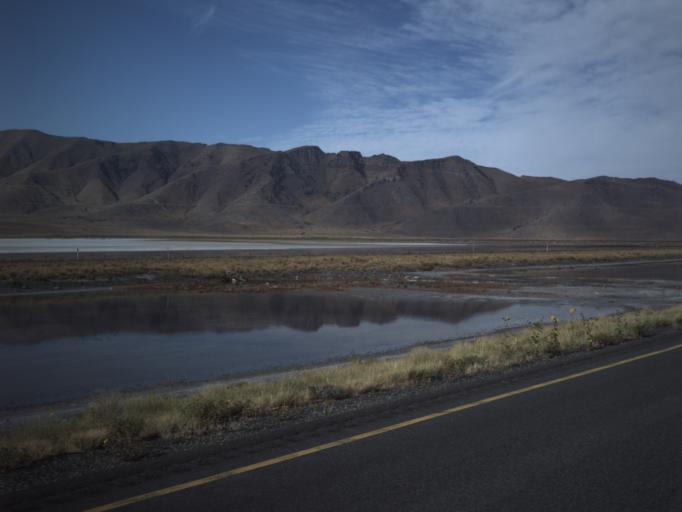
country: US
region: Utah
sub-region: Tooele County
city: Grantsville
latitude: 40.7206
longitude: -112.5550
